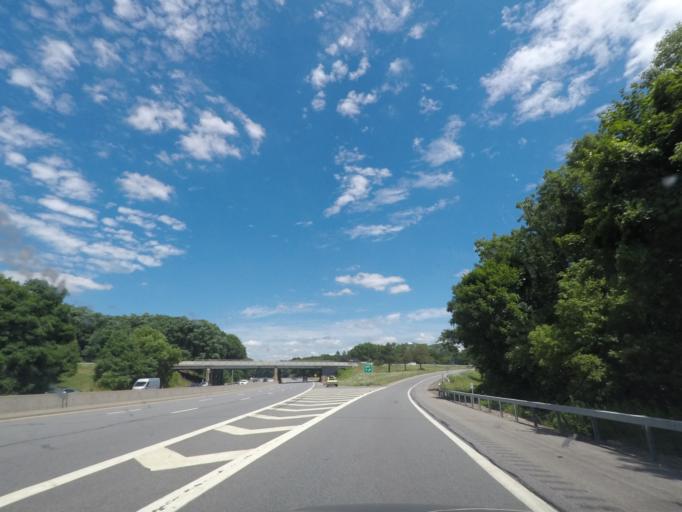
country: US
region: New York
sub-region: Schenectady County
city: Schenectady
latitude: 42.7809
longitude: -73.9233
